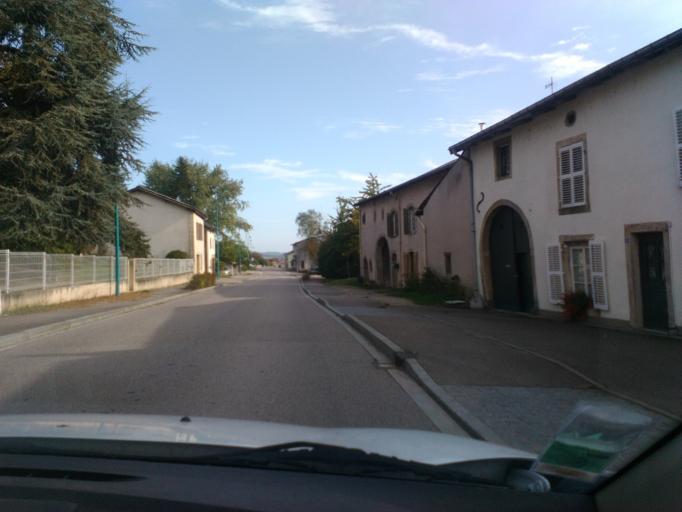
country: FR
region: Lorraine
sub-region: Departement des Vosges
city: Rambervillers
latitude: 48.3499
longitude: 6.5372
